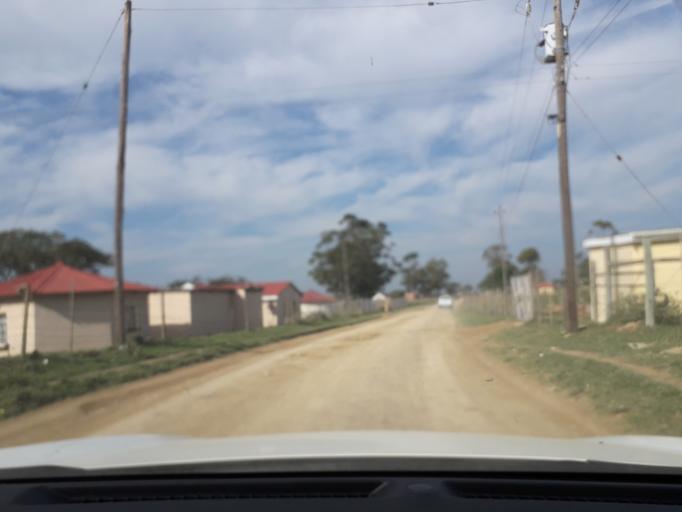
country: ZA
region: Eastern Cape
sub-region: Buffalo City Metropolitan Municipality
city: Bhisho
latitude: -33.0040
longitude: 27.3338
